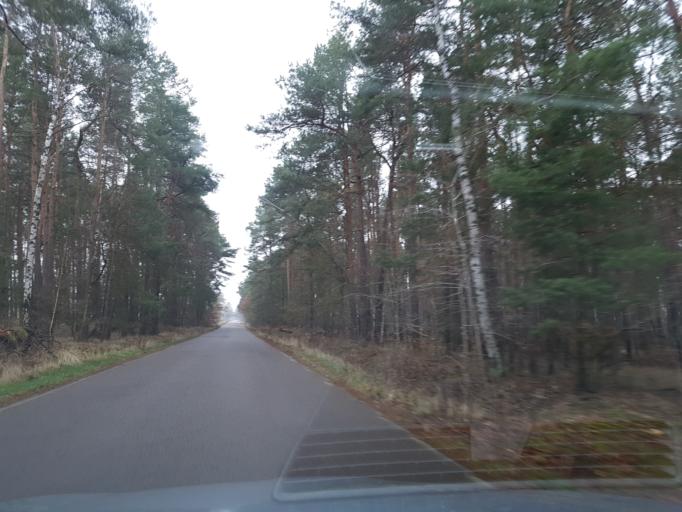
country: DE
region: Brandenburg
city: Schilda
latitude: 51.5984
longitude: 13.3866
